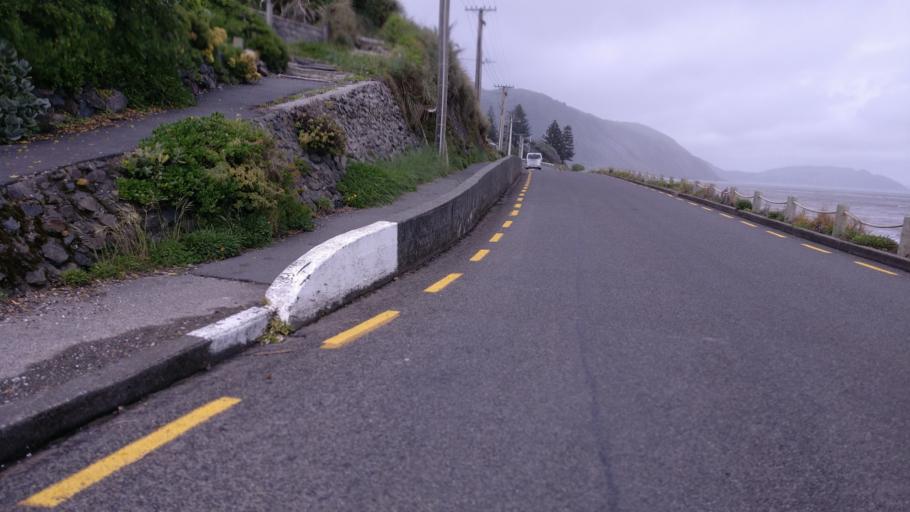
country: NZ
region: Wellington
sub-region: Kapiti Coast District
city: Paraparaumu
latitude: -40.9858
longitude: 174.9510
